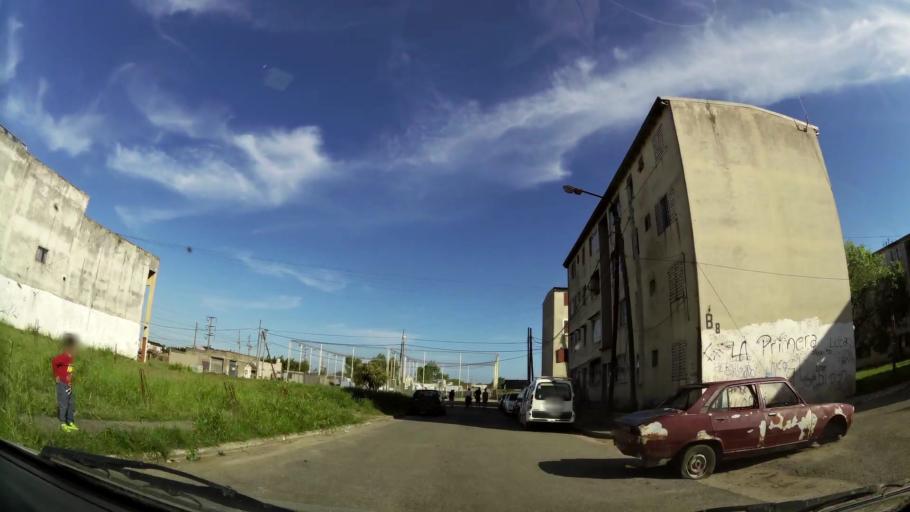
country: AR
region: Buenos Aires
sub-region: Partido de Quilmes
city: Quilmes
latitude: -34.7809
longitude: -58.2348
